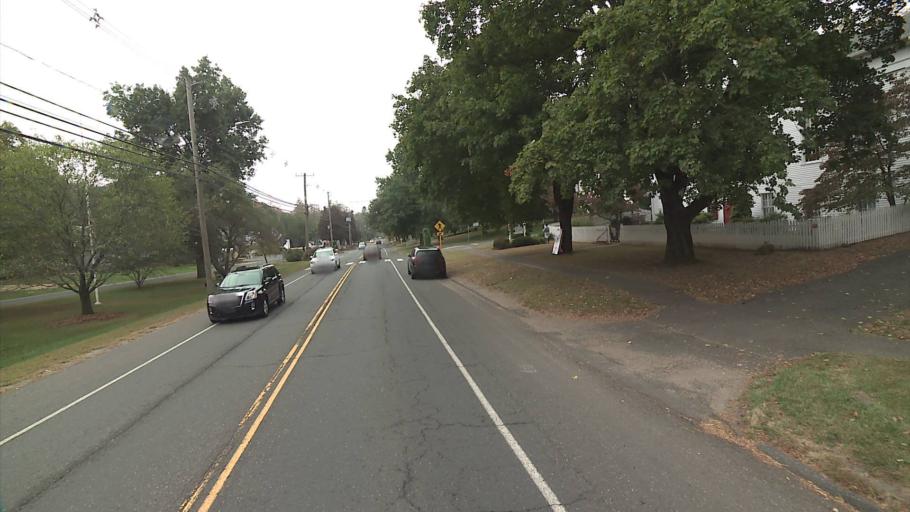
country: US
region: Connecticut
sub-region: Litchfield County
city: Woodbury Center
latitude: 41.5501
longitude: -73.2056
